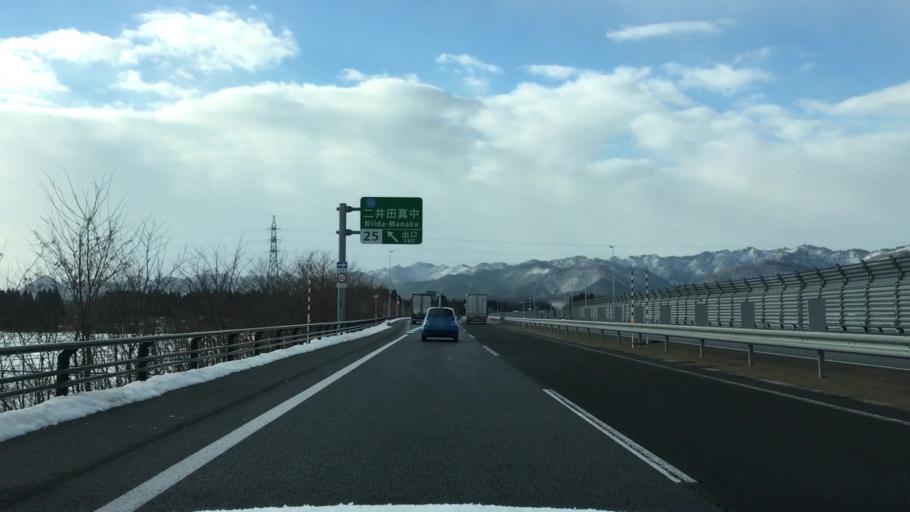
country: JP
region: Akita
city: Odate
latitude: 40.2539
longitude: 140.5191
